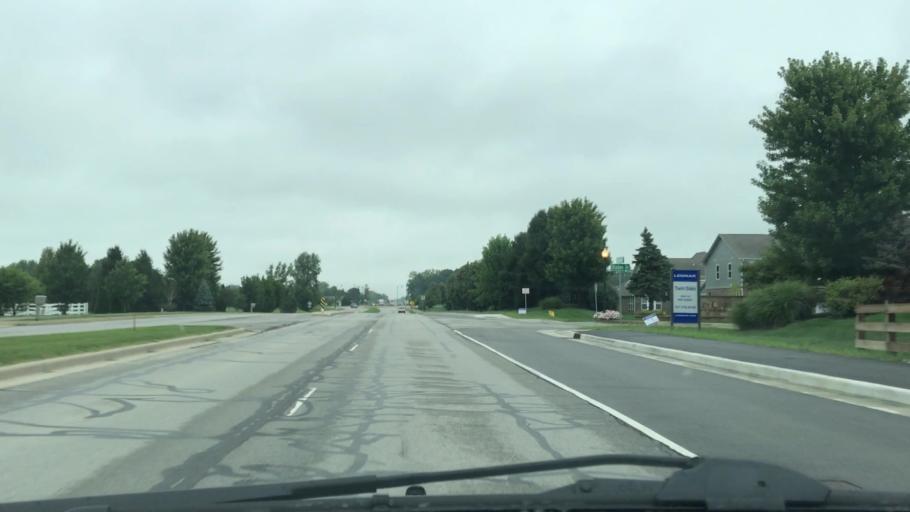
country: US
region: Indiana
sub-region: Hamilton County
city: Westfield
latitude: 40.0185
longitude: -86.0705
